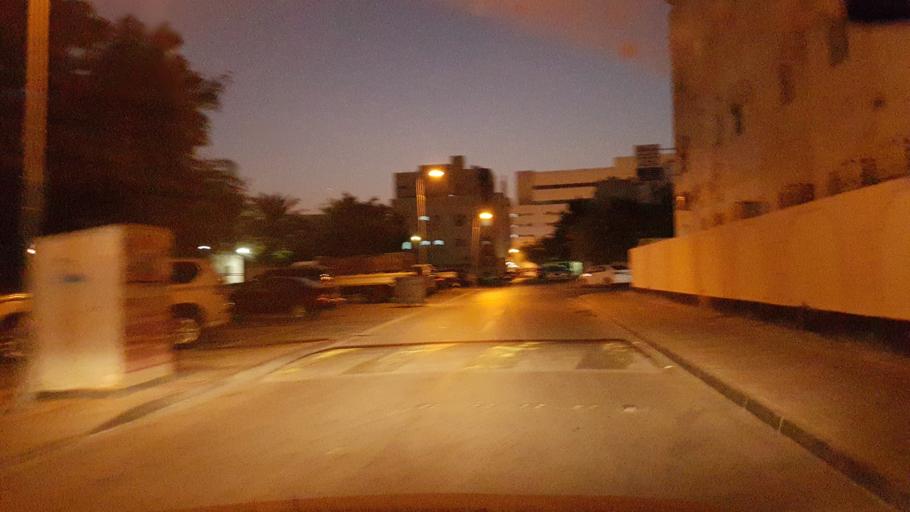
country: BH
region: Manama
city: Manama
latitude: 26.2214
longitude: 50.5800
